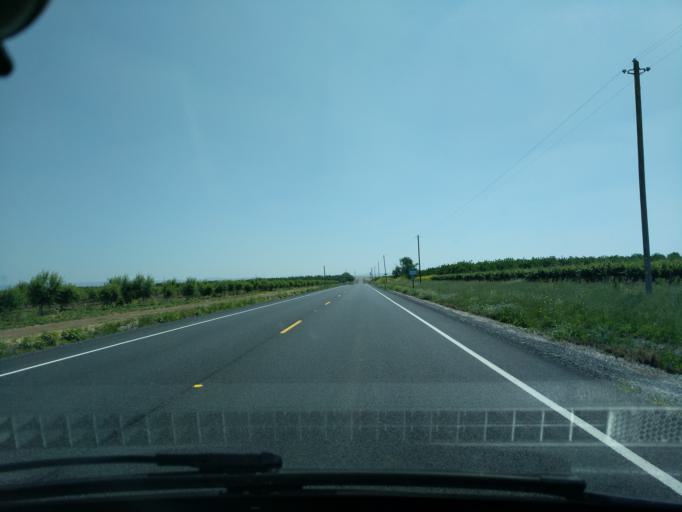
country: US
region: California
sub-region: San Joaquin County
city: Escalon
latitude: 37.9302
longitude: -120.9749
